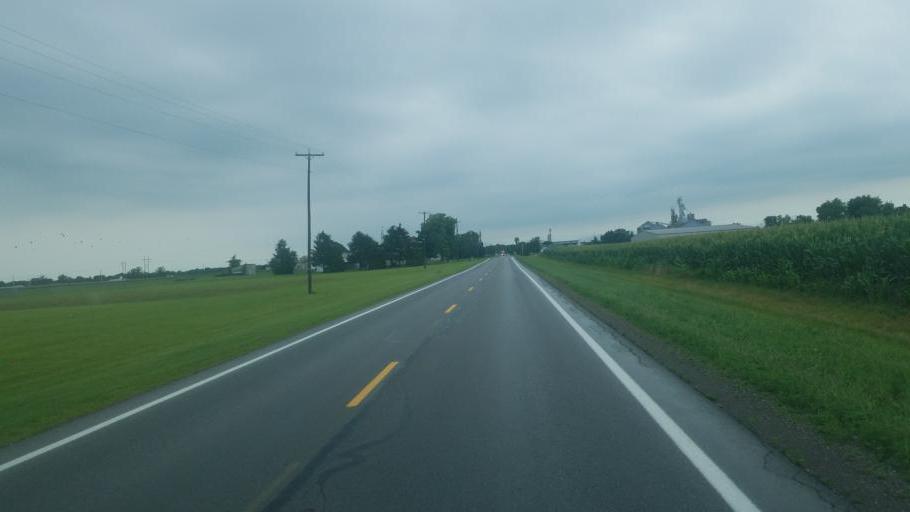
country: US
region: Ohio
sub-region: Hardin County
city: Kenton
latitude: 40.6215
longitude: -83.5973
